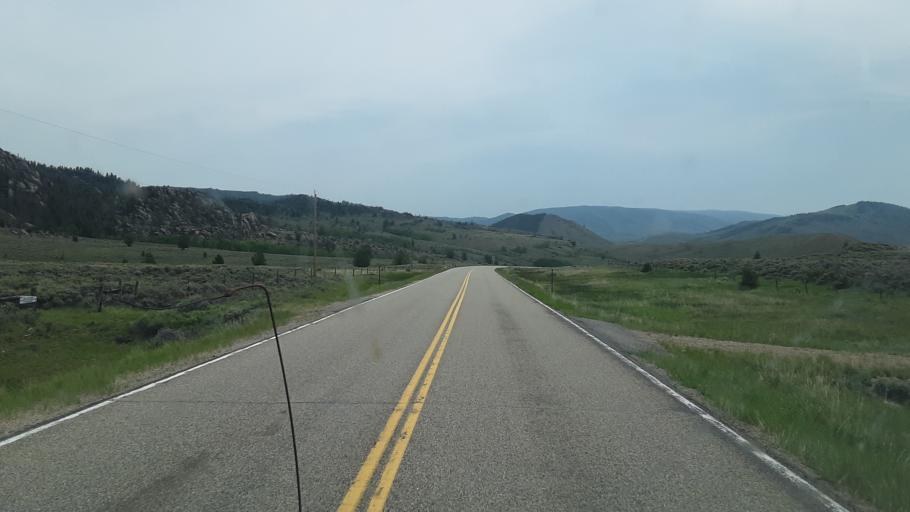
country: US
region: Colorado
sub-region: Jackson County
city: Walden
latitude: 40.9241
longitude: -106.3190
